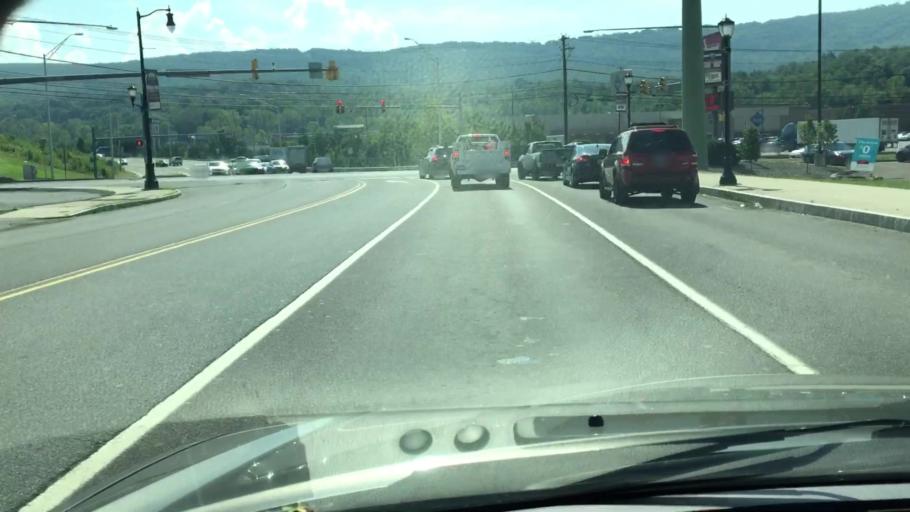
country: US
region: Pennsylvania
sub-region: Luzerne County
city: Georgetown
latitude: 41.2359
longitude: -75.8647
